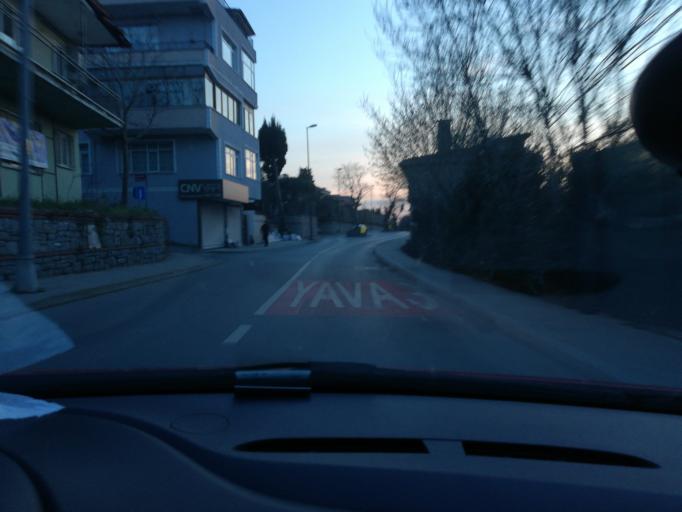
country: TR
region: Istanbul
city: UEskuedar
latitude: 41.0567
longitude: 29.0615
